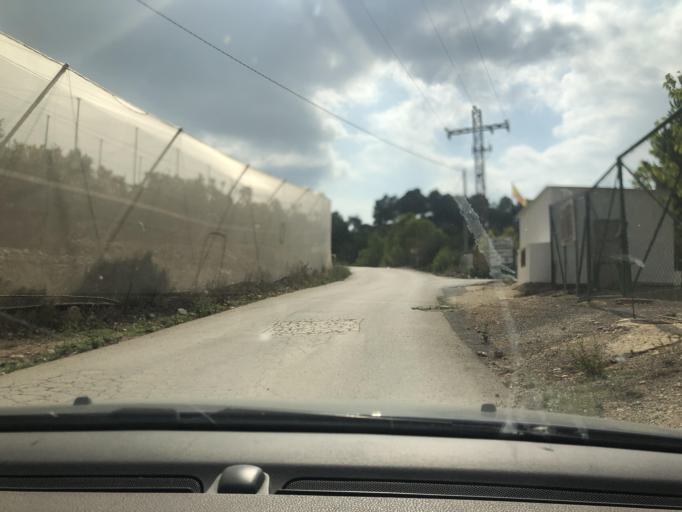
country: ES
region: Valencia
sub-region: Provincia de Alicante
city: Callosa d'En Sarria
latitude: 38.6547
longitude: -0.0926
